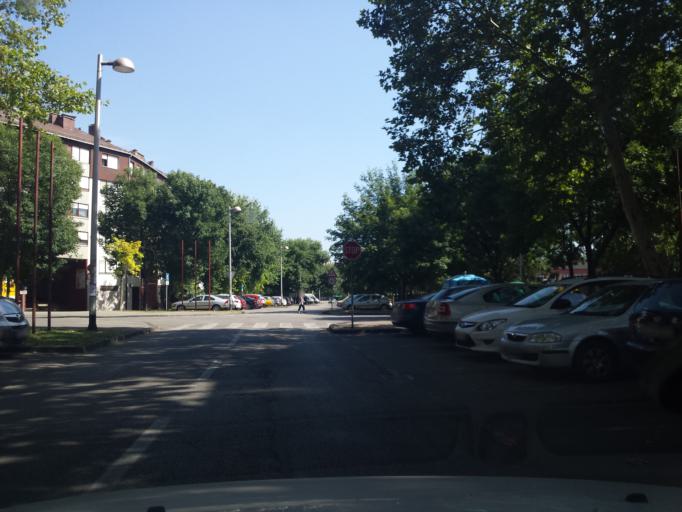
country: HR
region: Grad Zagreb
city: Jankomir
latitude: 45.7940
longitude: 15.9177
